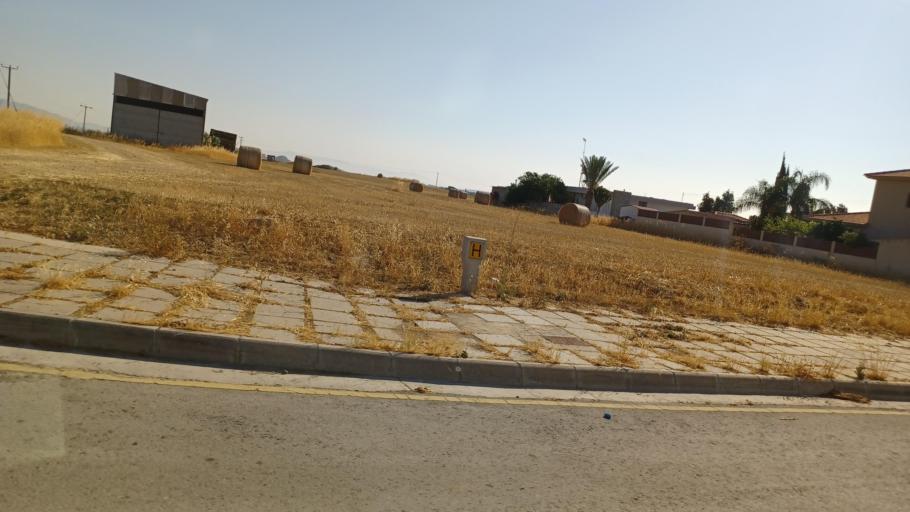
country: CY
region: Larnaka
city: Athienou
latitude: 35.0660
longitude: 33.5287
